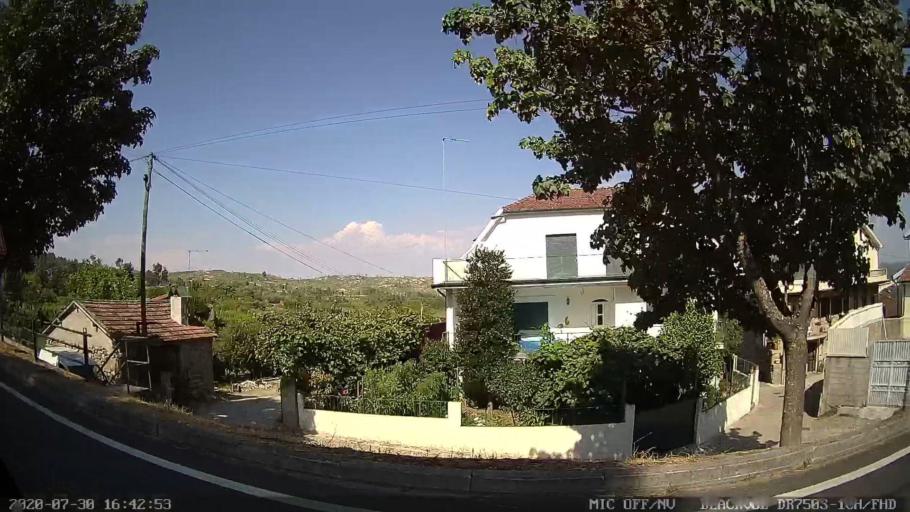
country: PT
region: Vila Real
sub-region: Sabrosa
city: Sabrosa
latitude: 41.2921
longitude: -7.4794
